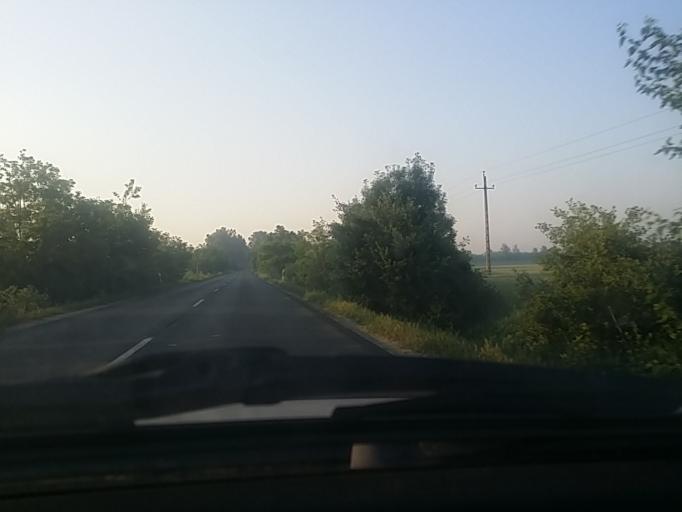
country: HU
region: Pest
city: Szentmartonkata
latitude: 47.4418
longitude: 19.7185
